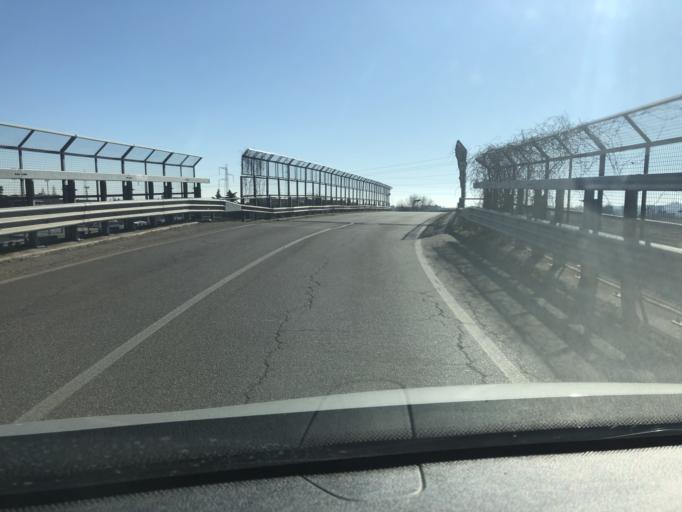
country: IT
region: Veneto
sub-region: Provincia di Verona
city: Bussolengo
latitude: 45.4545
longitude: 10.8616
